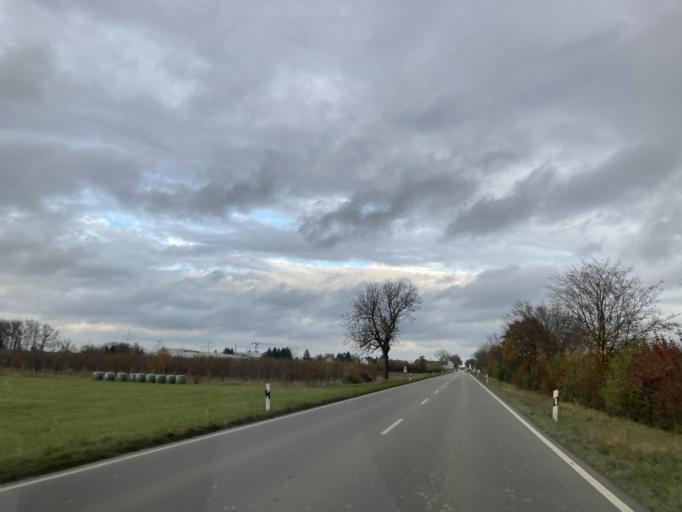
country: DE
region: Baden-Wuerttemberg
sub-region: Freiburg Region
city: Auggen
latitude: 47.7817
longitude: 7.5869
